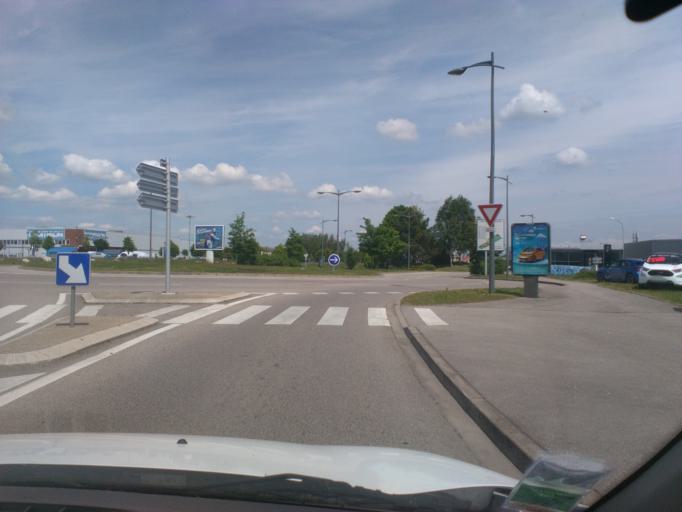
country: FR
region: Lorraine
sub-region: Departement des Vosges
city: Epinal
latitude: 48.1858
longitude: 6.4720
